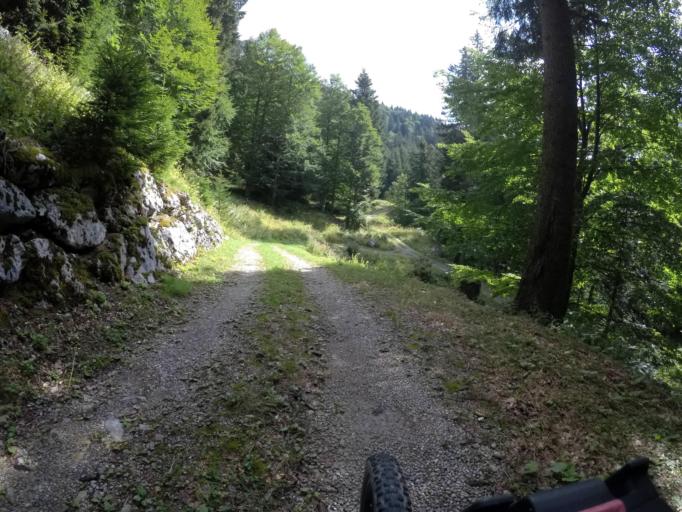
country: IT
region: Friuli Venezia Giulia
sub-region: Provincia di Udine
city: Paularo
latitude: 46.5115
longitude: 13.1919
